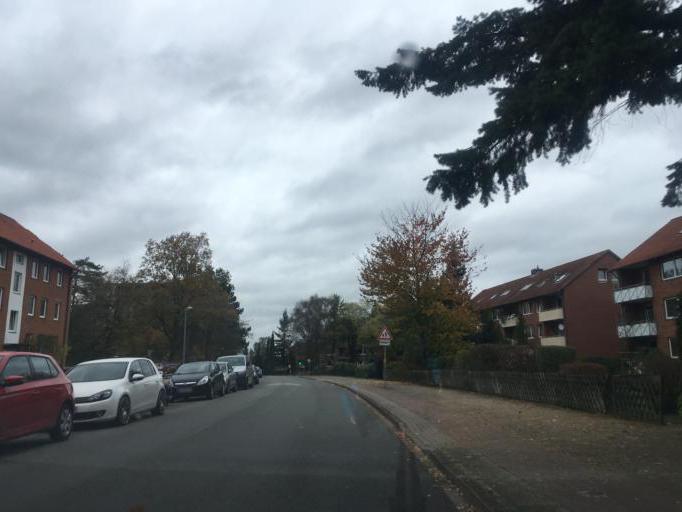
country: DE
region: Lower Saxony
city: Lueneburg
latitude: 53.2610
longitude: 10.4032
